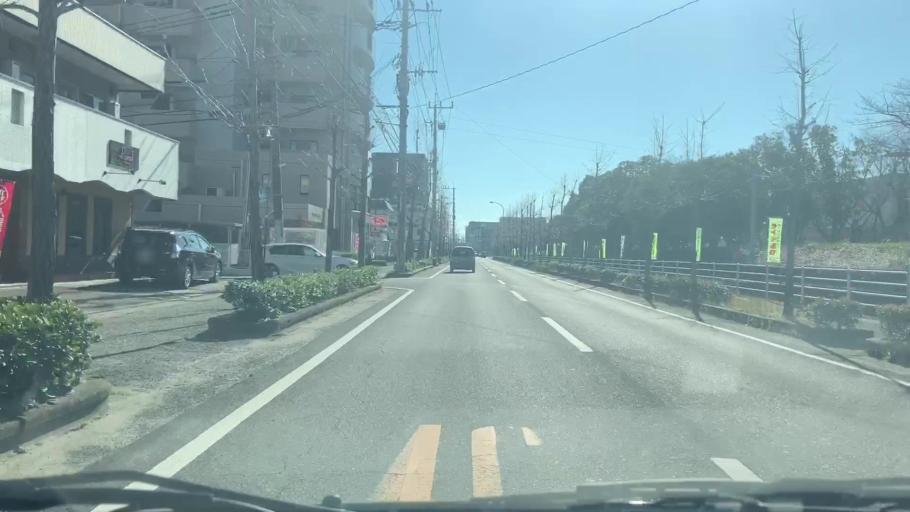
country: JP
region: Saga Prefecture
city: Saga-shi
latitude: 33.2856
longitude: 130.2684
